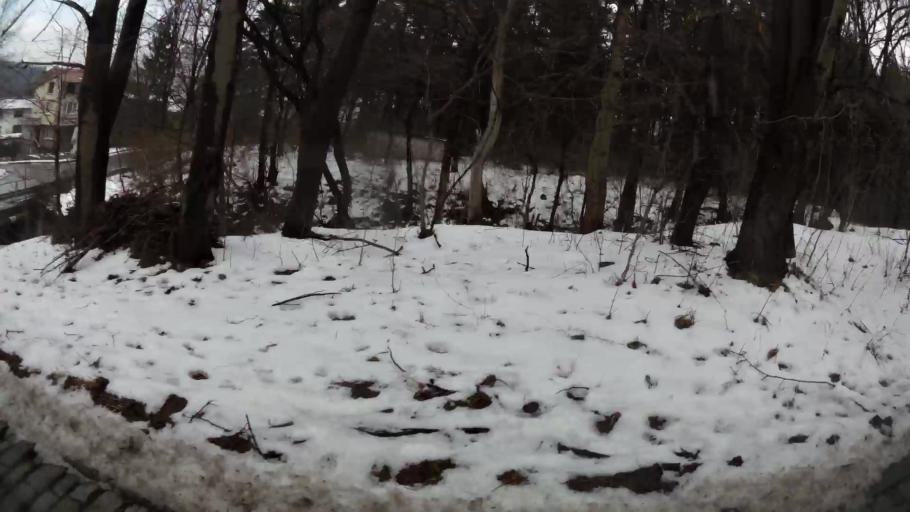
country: BG
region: Sofia-Capital
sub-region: Stolichna Obshtina
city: Sofia
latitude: 42.6558
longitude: 23.2378
